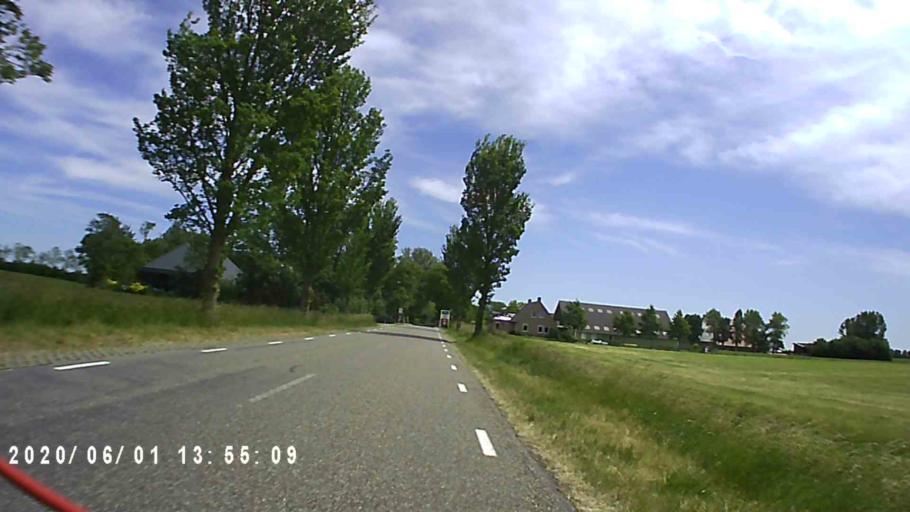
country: NL
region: Friesland
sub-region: Gemeente Littenseradiel
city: Makkum
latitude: 53.1027
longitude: 5.6388
